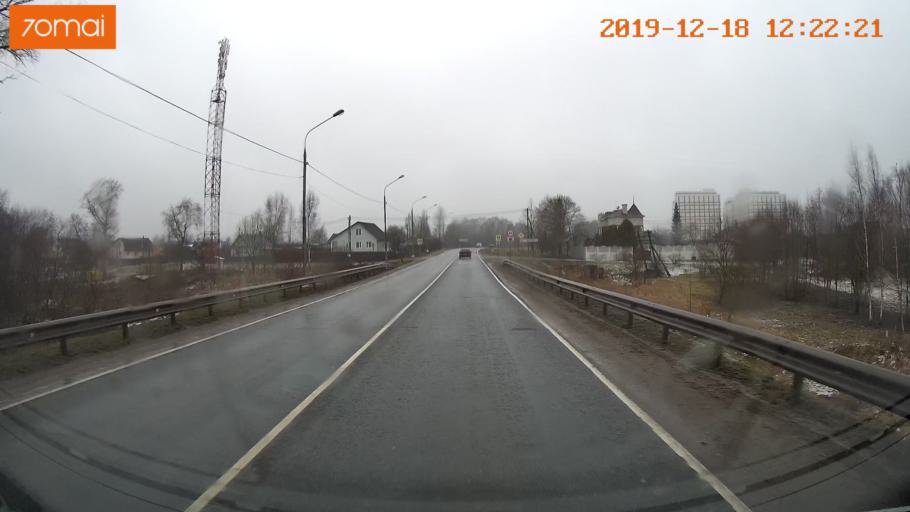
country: RU
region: Moskovskaya
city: Novopetrovskoye
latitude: 56.0051
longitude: 36.4799
